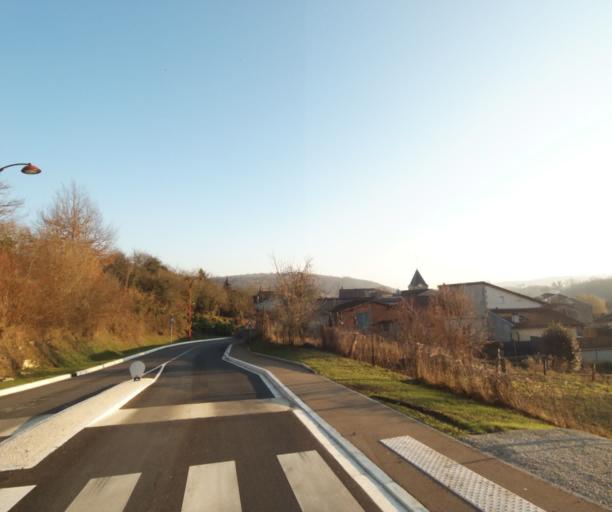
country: FR
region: Champagne-Ardenne
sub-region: Departement de la Haute-Marne
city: Chevillon
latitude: 48.5451
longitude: 5.1018
